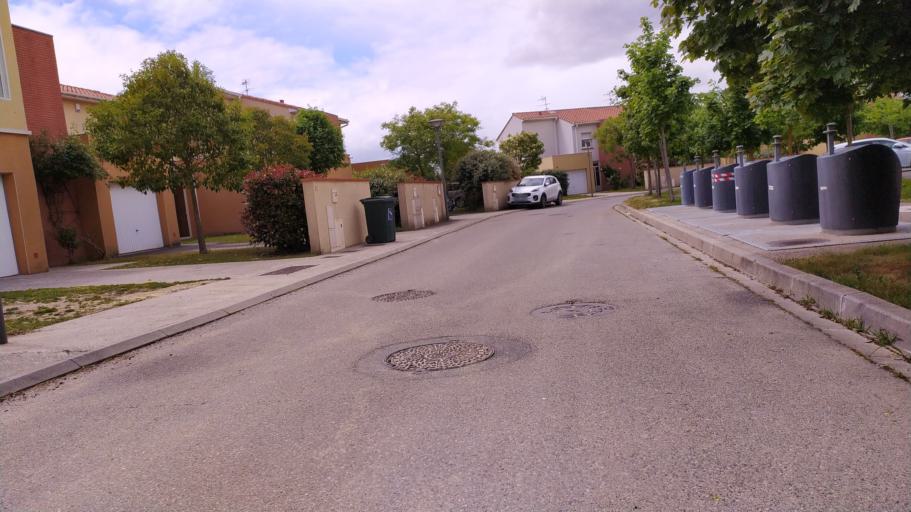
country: FR
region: Midi-Pyrenees
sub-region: Departement de la Haute-Garonne
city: La Salvetat-Saint-Gilles
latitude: 43.5823
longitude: 1.2861
